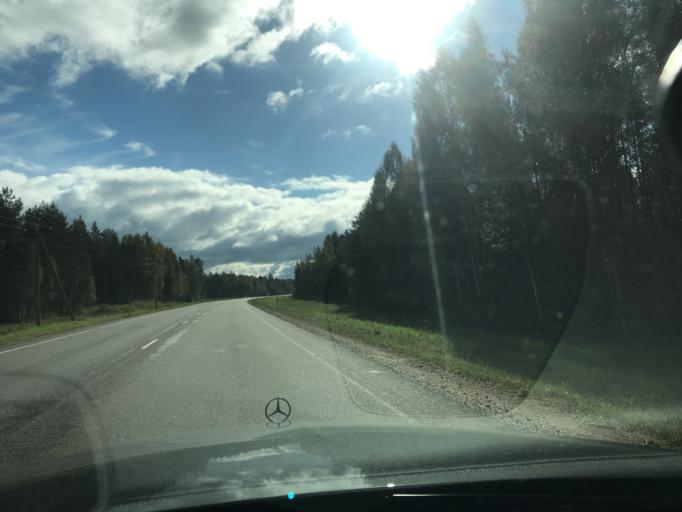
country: EE
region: Vorumaa
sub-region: Voru linn
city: Voru
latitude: 57.8367
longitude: 27.0585
